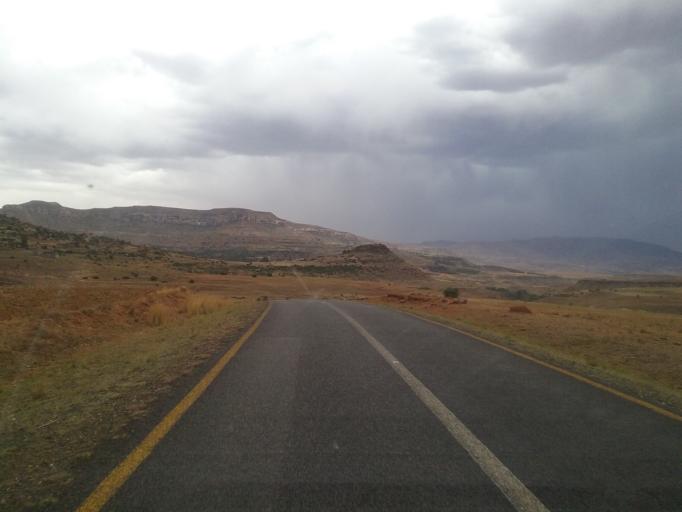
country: LS
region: Quthing
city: Quthing
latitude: -30.2934
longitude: 27.8126
